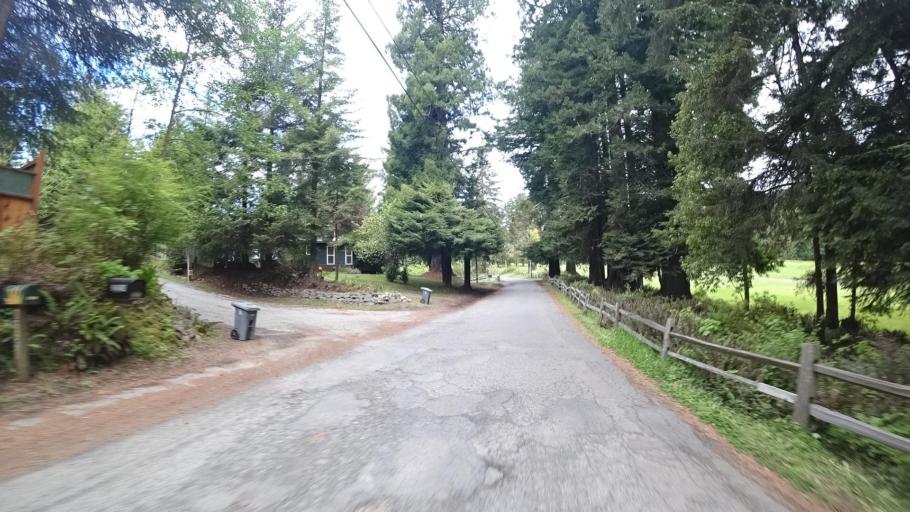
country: US
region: California
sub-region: Humboldt County
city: Bayside
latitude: 40.8464
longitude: -124.0538
